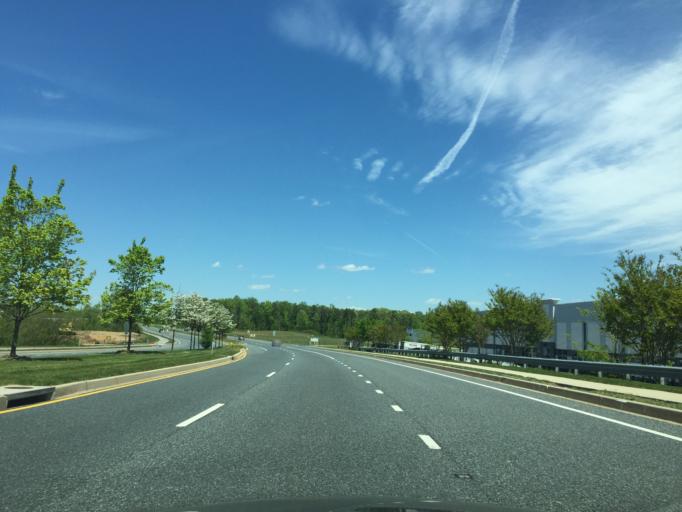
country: US
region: Maryland
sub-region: Baltimore County
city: Bowleys Quarters
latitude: 39.3478
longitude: -76.4118
